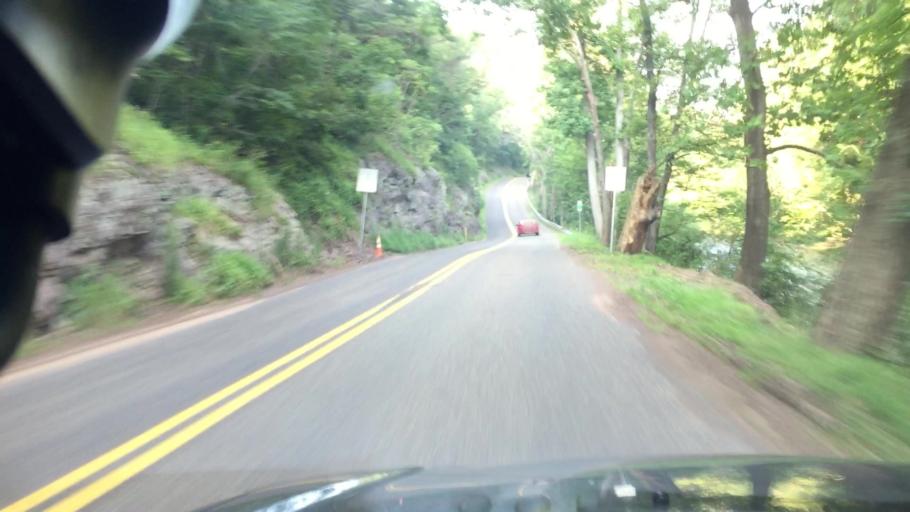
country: US
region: Pennsylvania
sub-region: Columbia County
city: Catawissa
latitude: 40.9673
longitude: -76.4270
